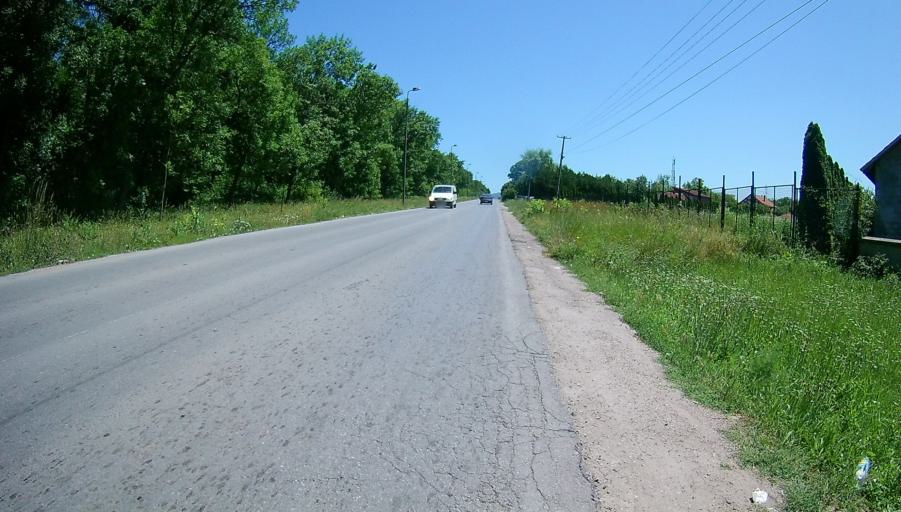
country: RS
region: Central Serbia
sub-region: Nisavski Okrug
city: Nis
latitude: 43.3043
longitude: 21.8688
